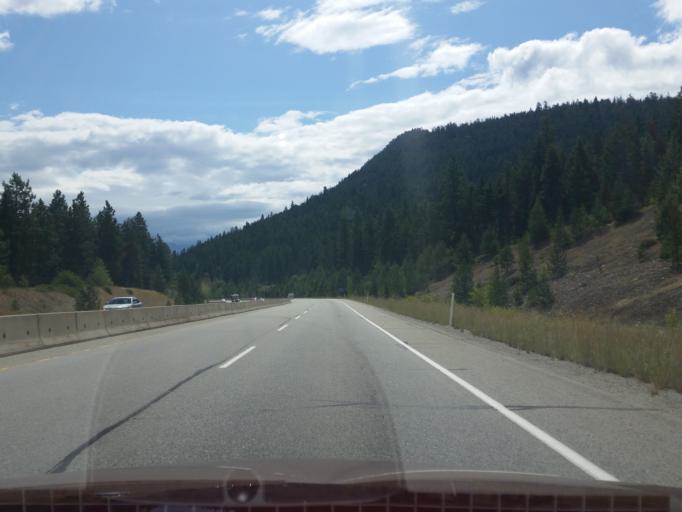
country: CA
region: British Columbia
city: Peachland
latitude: 49.8197
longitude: -119.7822
